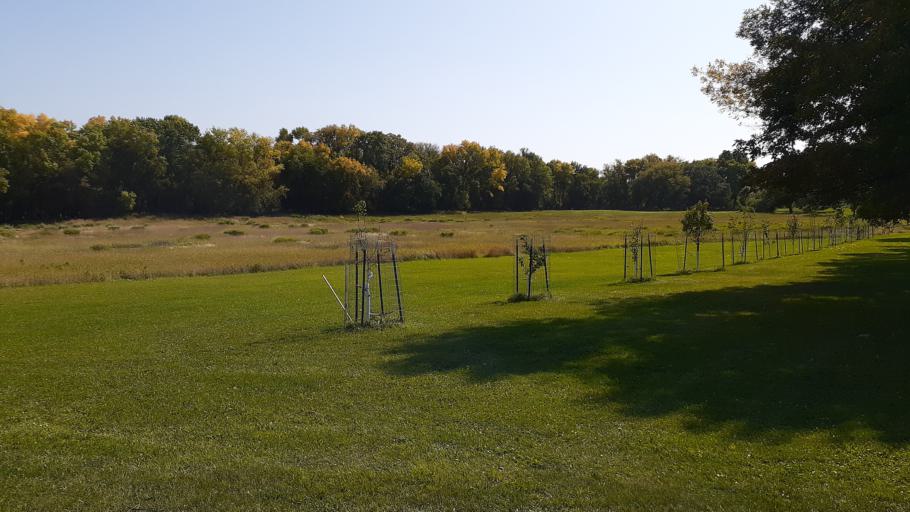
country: US
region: Minnesota
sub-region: Clay County
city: Oakport
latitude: 46.9109
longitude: -96.7660
